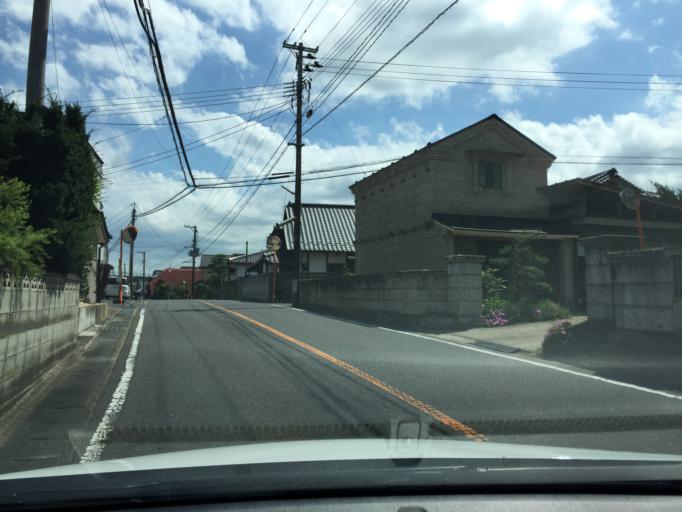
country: JP
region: Fukushima
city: Koriyama
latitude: 37.3514
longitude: 140.2746
